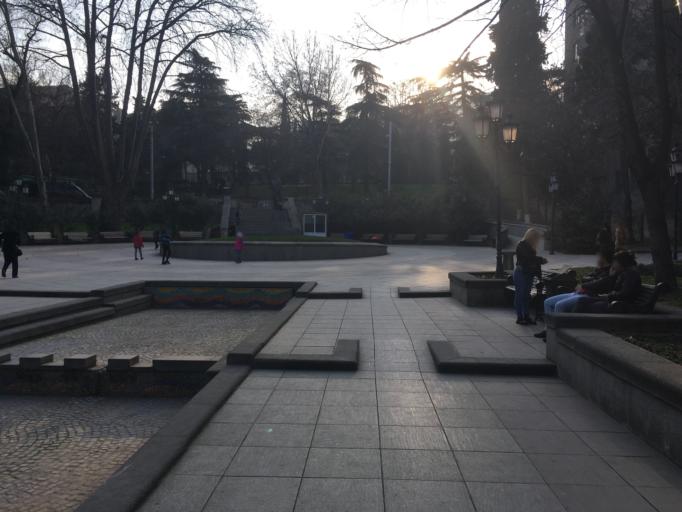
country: GE
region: T'bilisi
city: Tbilisi
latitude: 41.6992
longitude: 44.8007
